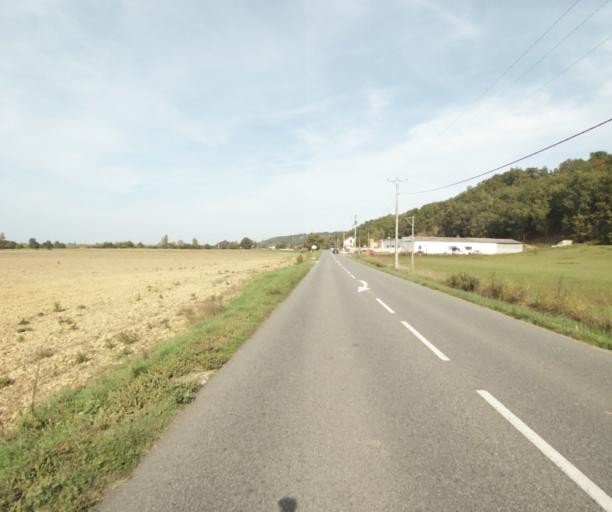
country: FR
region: Midi-Pyrenees
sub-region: Departement du Tarn-et-Garonne
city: Corbarieu
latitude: 43.9502
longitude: 1.3646
